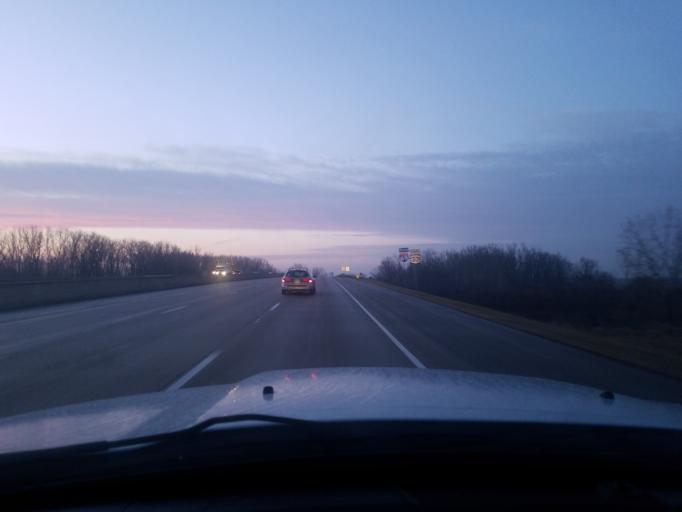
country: US
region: Indiana
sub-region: Huntington County
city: Roanoke
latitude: 41.0245
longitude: -85.2526
